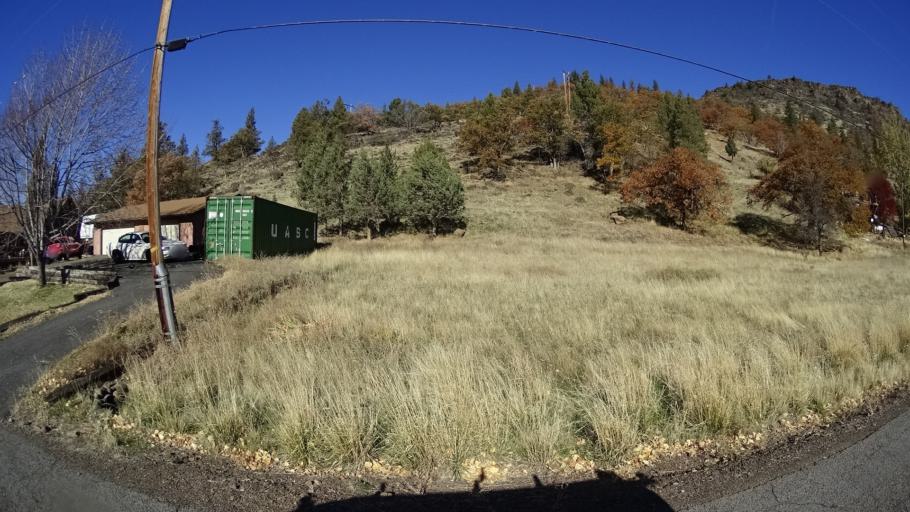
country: US
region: California
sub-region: Siskiyou County
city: Montague
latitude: 41.9662
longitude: -122.2639
